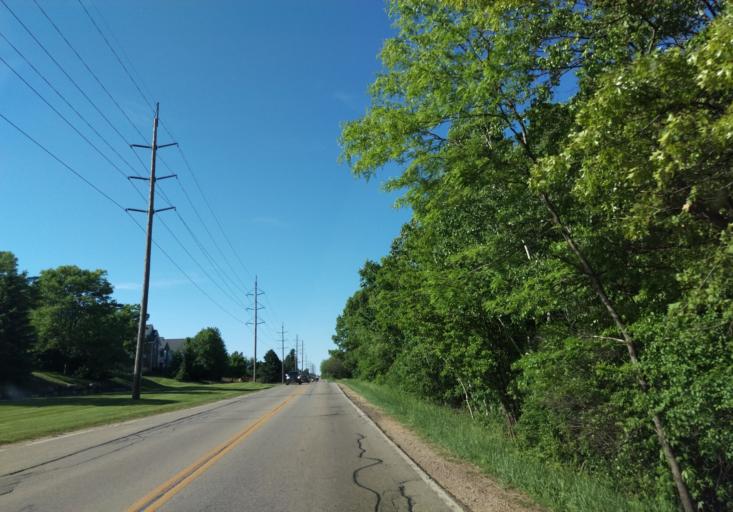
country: US
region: Wisconsin
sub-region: Dane County
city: Middleton
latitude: 43.0802
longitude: -89.5368
